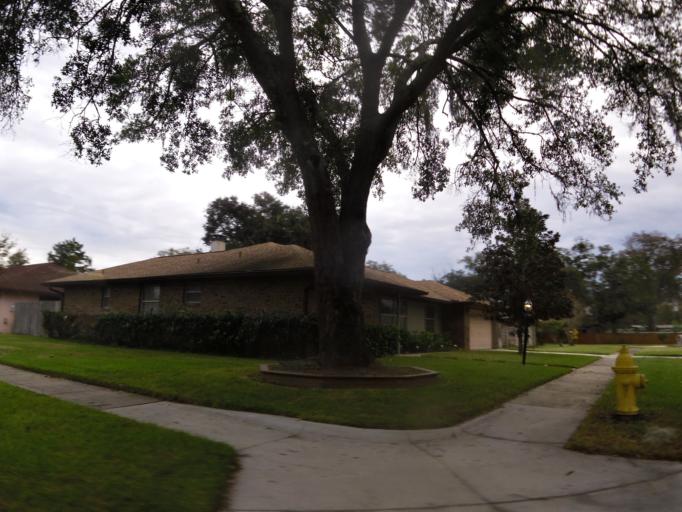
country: US
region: Florida
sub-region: Duval County
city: Jacksonville
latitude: 30.2665
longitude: -81.5992
